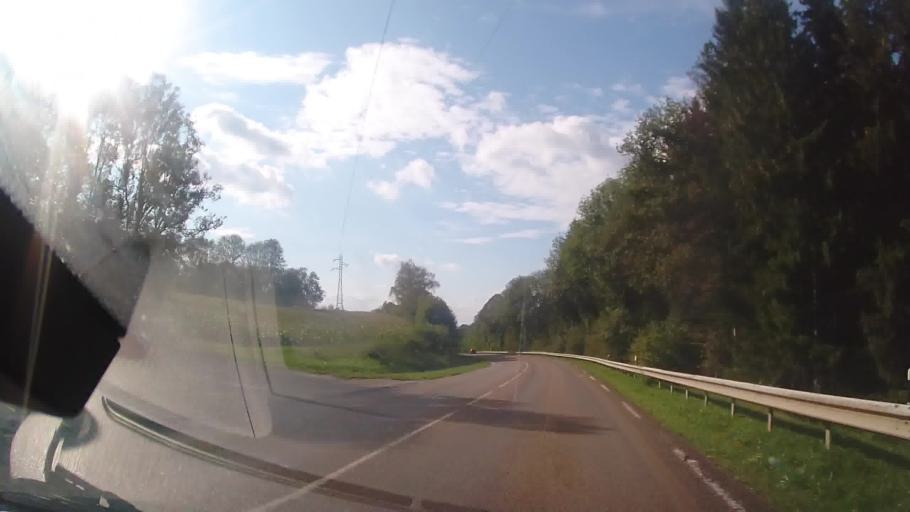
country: FR
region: Franche-Comte
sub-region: Departement du Jura
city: Clairvaux-les-Lacs
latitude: 46.5851
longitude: 5.7643
